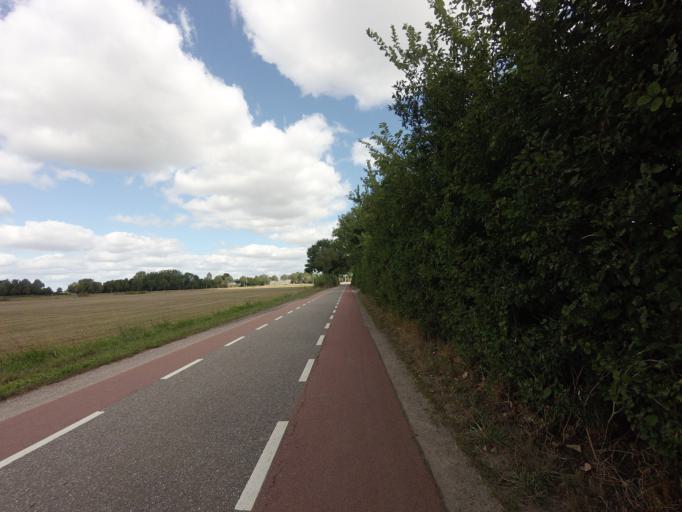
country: NL
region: North Brabant
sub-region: Gemeente Landerd
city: Schaijk
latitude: 51.7997
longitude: 5.6188
